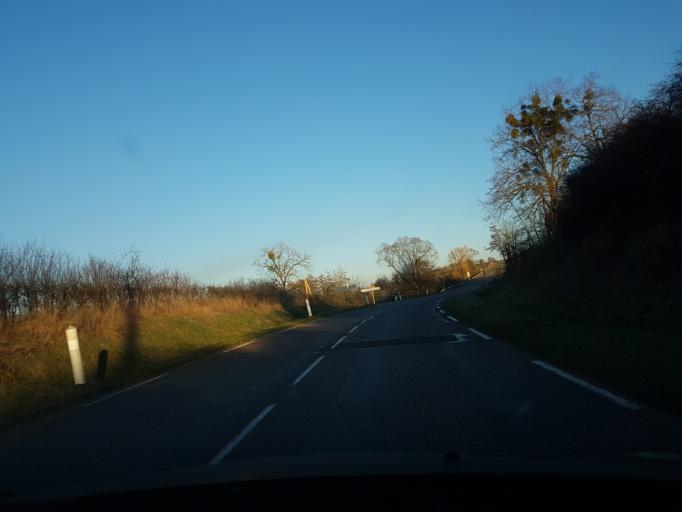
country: FR
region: Lorraine
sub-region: Departement des Vosges
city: Darney
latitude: 47.9332
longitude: 6.0693
